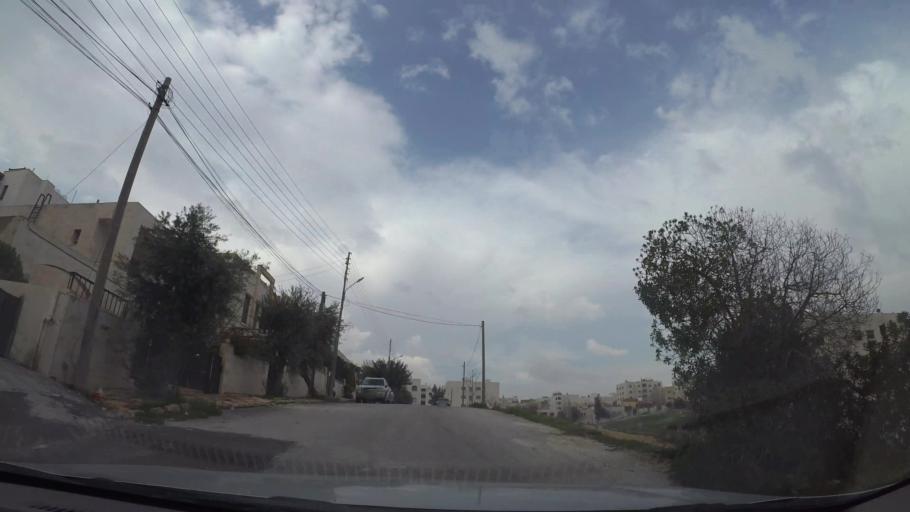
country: JO
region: Amman
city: Umm as Summaq
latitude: 31.8835
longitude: 35.8637
